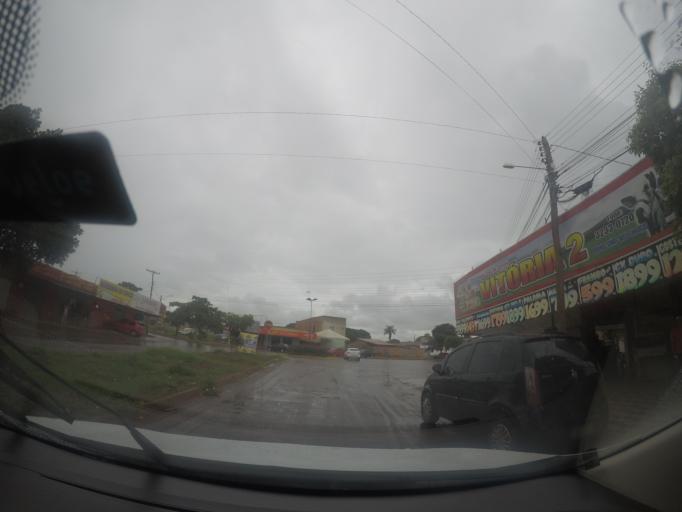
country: BR
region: Goias
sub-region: Trindade
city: Trindade
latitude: -16.6412
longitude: -49.4351
